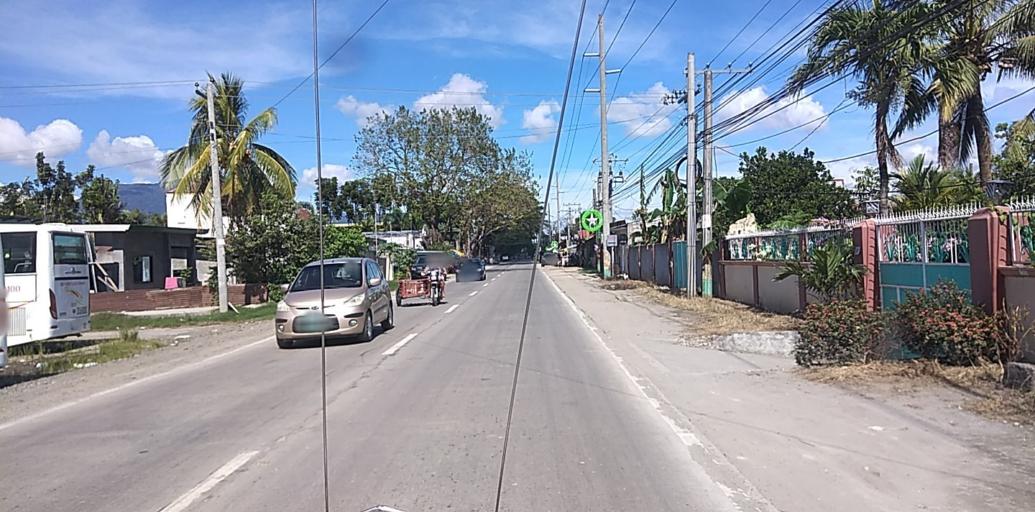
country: PH
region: Central Luzon
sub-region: Province of Pampanga
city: Santa Ana
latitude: 15.1200
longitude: 120.7758
